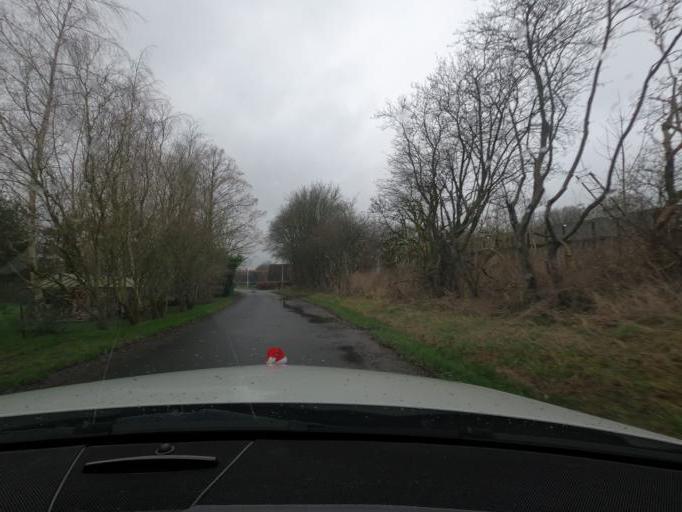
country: DK
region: South Denmark
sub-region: Haderslev Kommune
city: Starup
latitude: 55.2466
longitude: 9.6840
